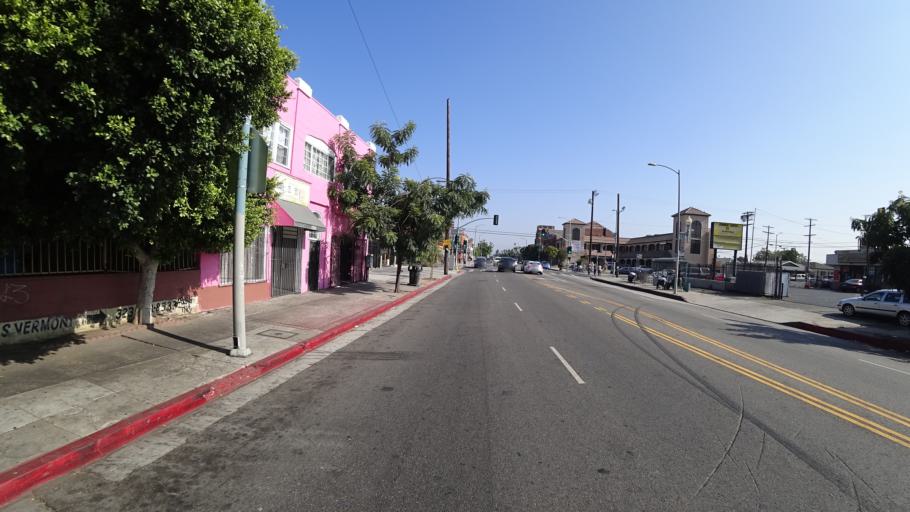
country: US
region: California
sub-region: Los Angeles County
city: Westmont
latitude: 33.9927
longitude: -118.2916
